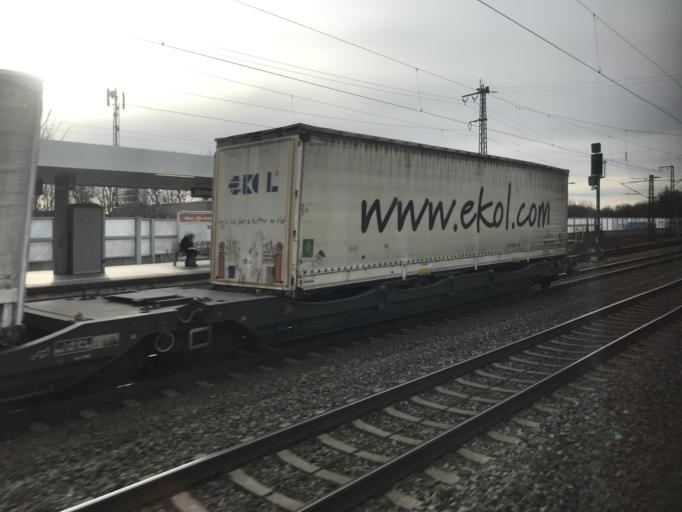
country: DE
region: Bavaria
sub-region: Upper Bavaria
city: Olching
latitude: 48.2104
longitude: 11.3348
